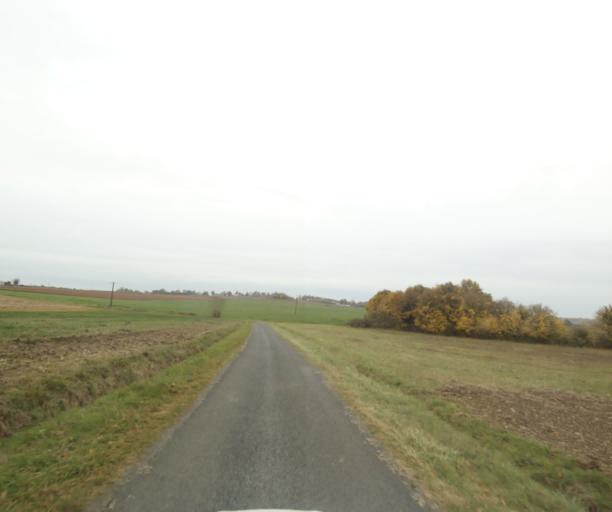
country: FR
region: Poitou-Charentes
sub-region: Departement de la Charente-Maritime
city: Chermignac
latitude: 45.7311
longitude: -0.6774
